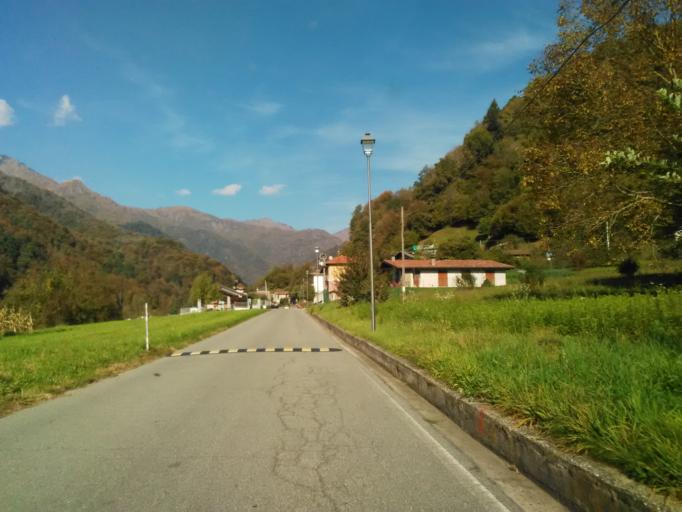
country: IT
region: Piedmont
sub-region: Provincia di Vercelli
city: Postua
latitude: 45.7167
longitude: 8.2256
